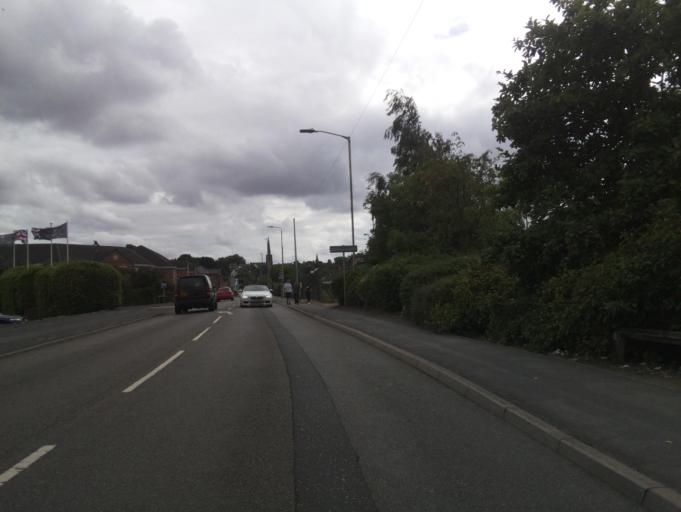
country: GB
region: England
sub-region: Leicestershire
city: Castle Donington
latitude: 52.8480
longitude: -1.3369
